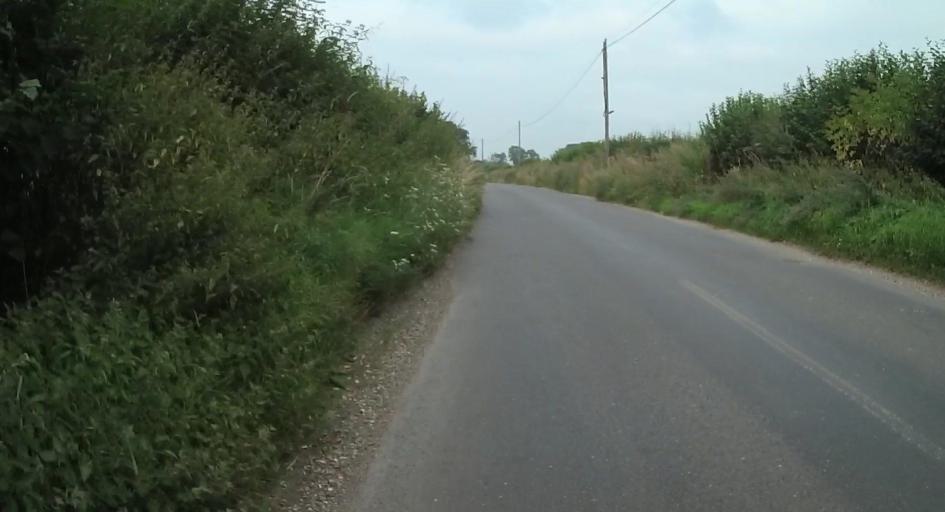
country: GB
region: England
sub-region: Hampshire
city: Old Basing
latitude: 51.2197
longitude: -1.0123
